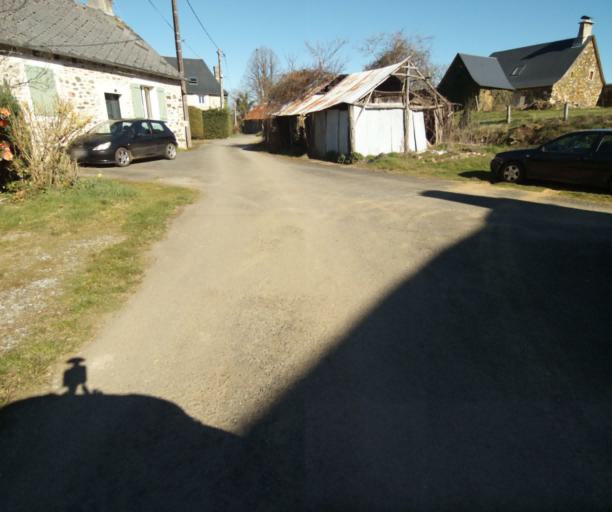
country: FR
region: Limousin
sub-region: Departement de la Correze
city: Seilhac
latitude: 45.3961
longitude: 1.7084
